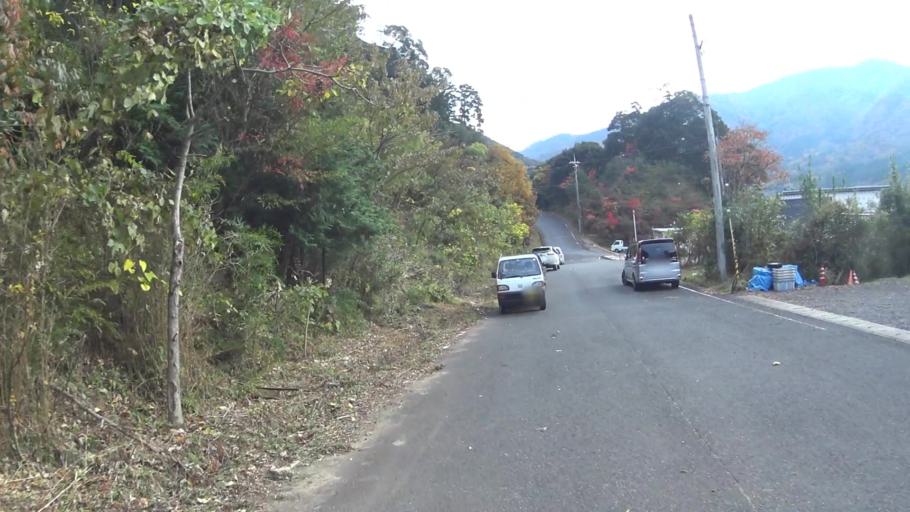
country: JP
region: Kyoto
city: Maizuru
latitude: 35.5718
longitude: 135.4283
